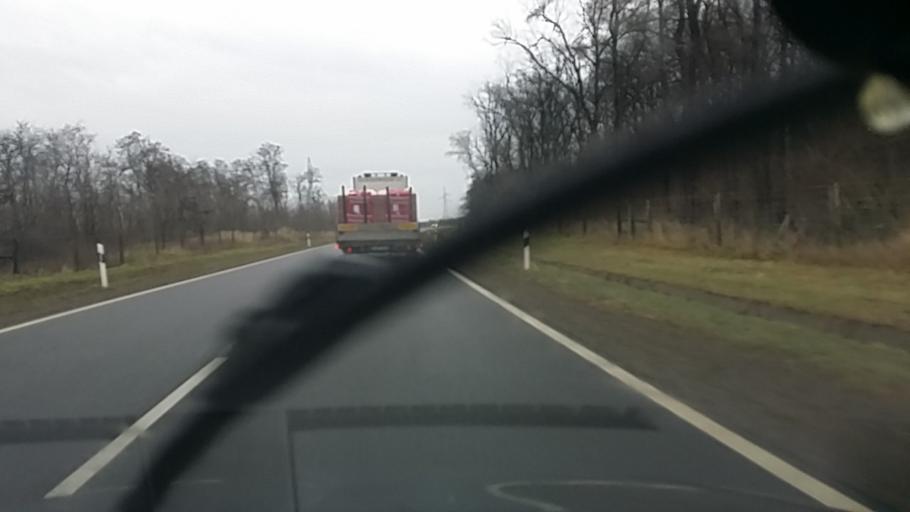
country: HU
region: Hajdu-Bihar
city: Hajduhadhaz
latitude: 47.6348
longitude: 21.6472
